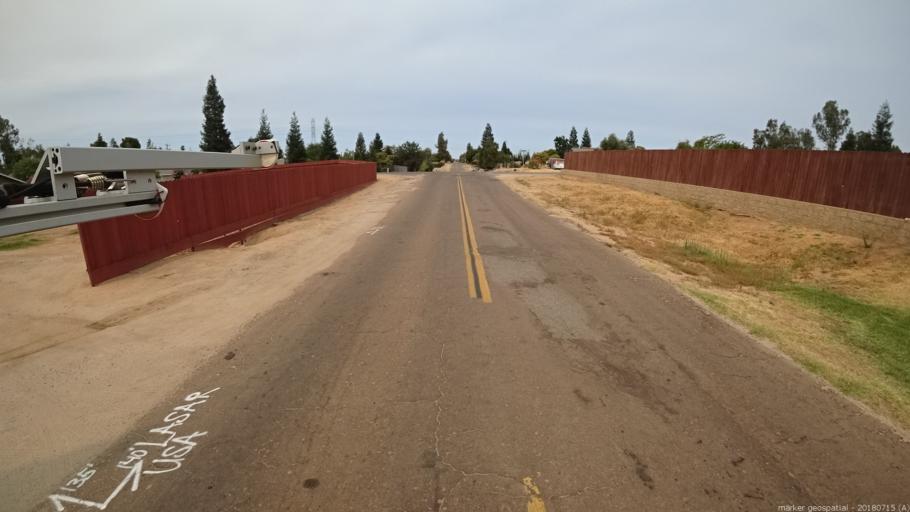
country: US
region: California
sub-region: Madera County
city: Madera Acres
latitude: 37.0182
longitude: -120.0792
